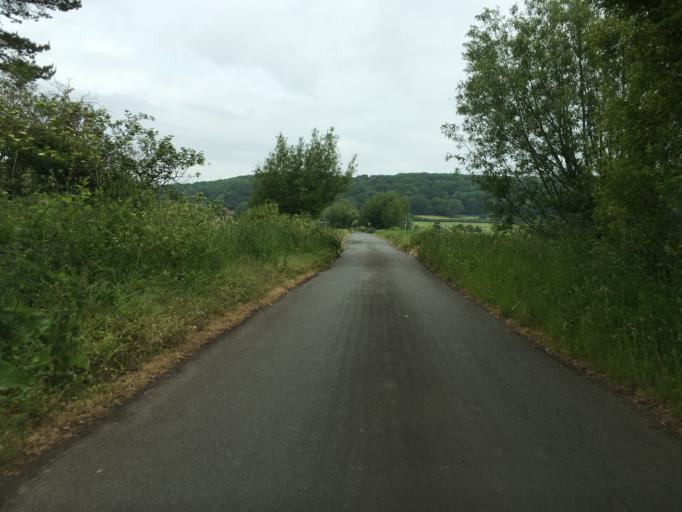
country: GB
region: England
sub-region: North Somerset
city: Clevedon
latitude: 51.4515
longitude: -2.8196
